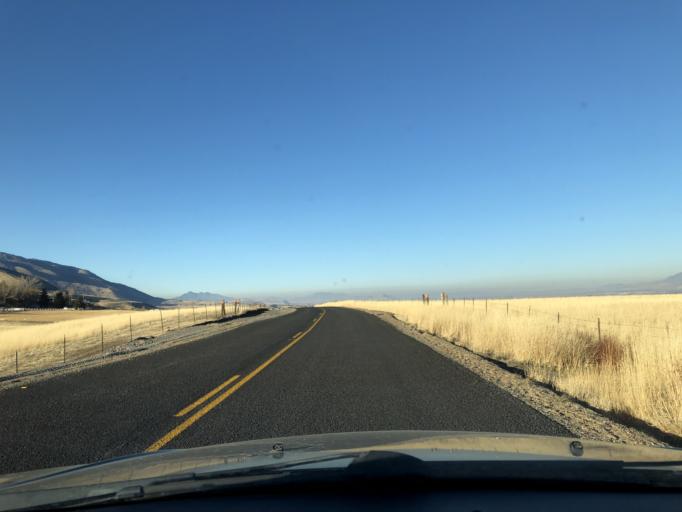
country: US
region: Utah
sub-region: Cache County
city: Wellsville
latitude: 41.5921
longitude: -111.9269
